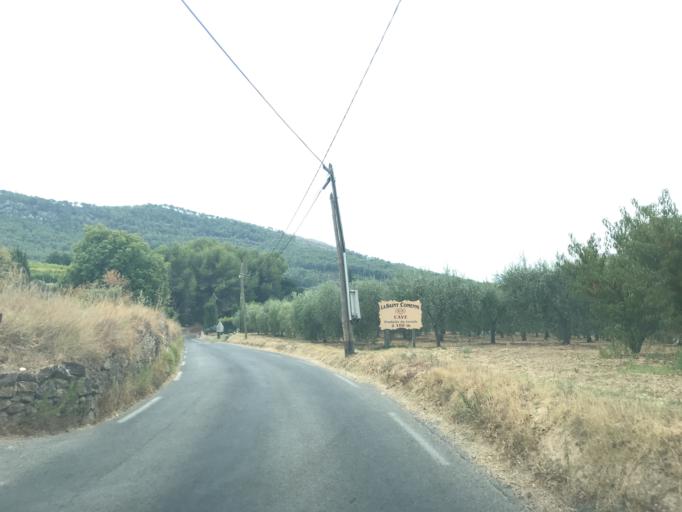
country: FR
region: Provence-Alpes-Cote d'Azur
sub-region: Departement du Var
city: Saint-Cyr-sur-Mer
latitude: 43.1778
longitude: 5.7300
